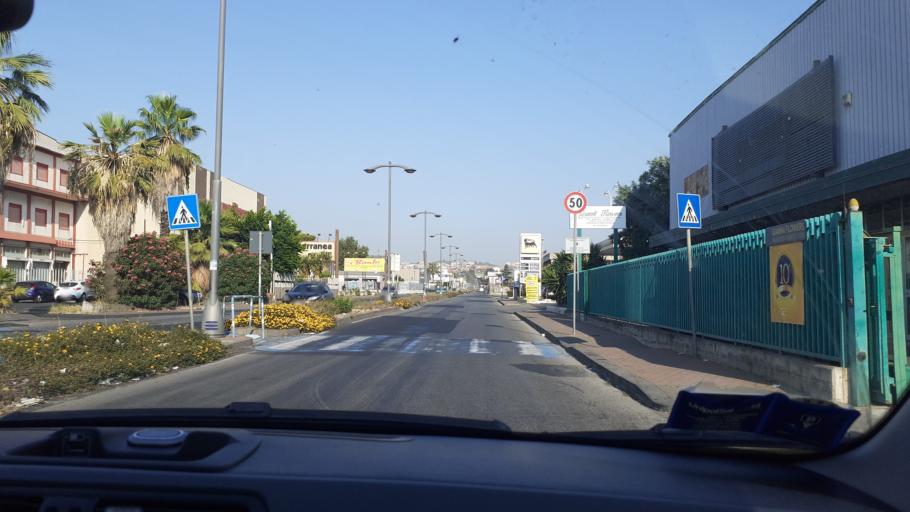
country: IT
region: Sicily
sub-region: Catania
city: Misterbianco
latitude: 37.5121
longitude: 15.0316
